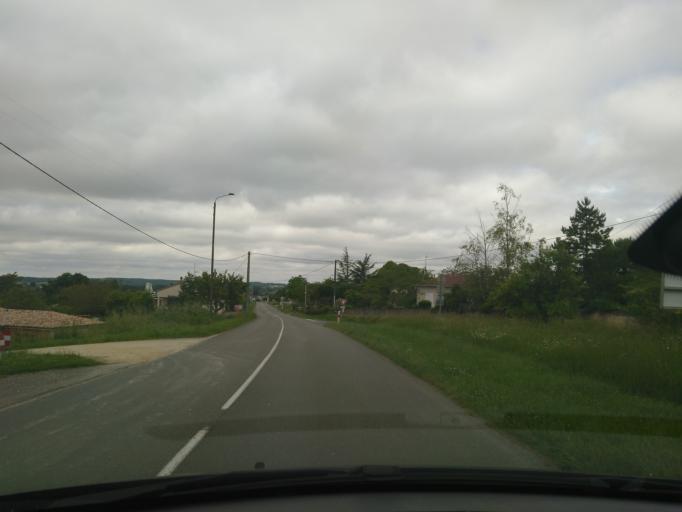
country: FR
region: Aquitaine
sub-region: Departement du Lot-et-Garonne
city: Cancon
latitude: 44.5384
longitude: 0.6184
